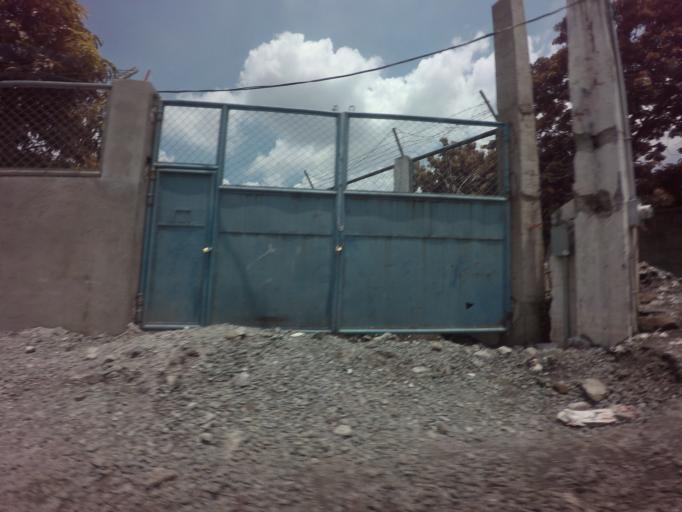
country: PH
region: Calabarzon
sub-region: Province of Laguna
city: San Pedro
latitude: 14.3854
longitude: 121.0511
